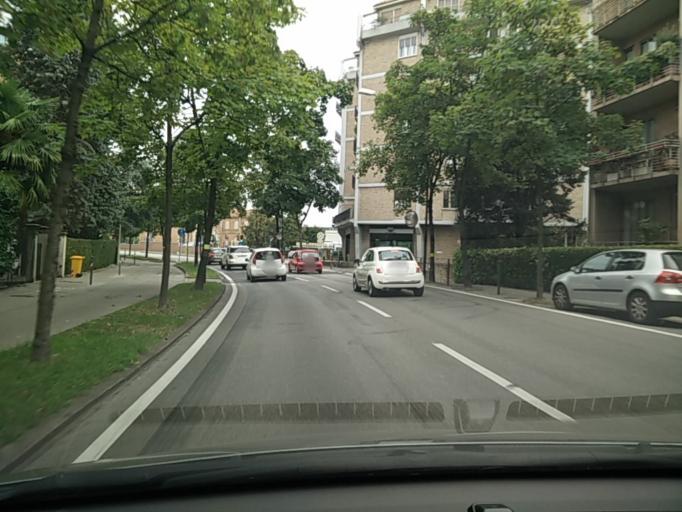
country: IT
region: Veneto
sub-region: Provincia di Treviso
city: Treviso
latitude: 45.6608
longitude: 12.2386
